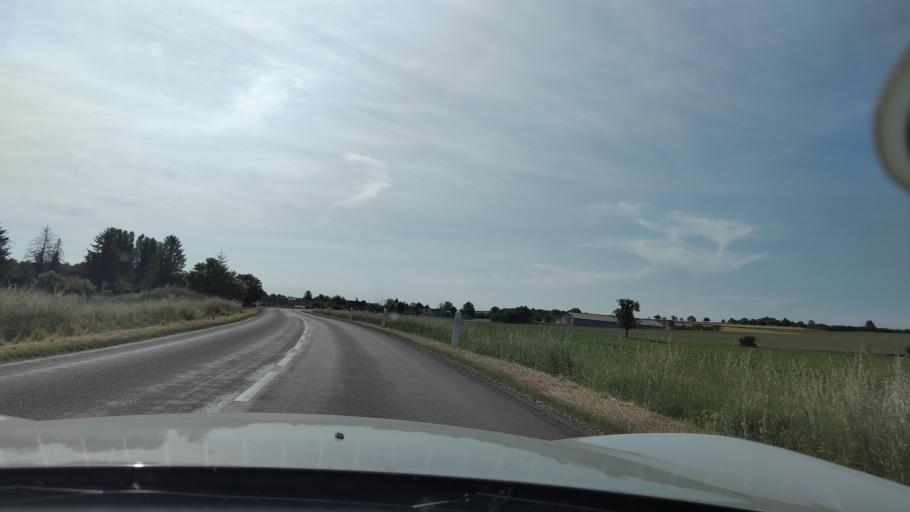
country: FR
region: Champagne-Ardenne
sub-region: Departement de l'Aube
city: Marigny-le-Chatel
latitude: 48.4436
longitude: 3.6437
